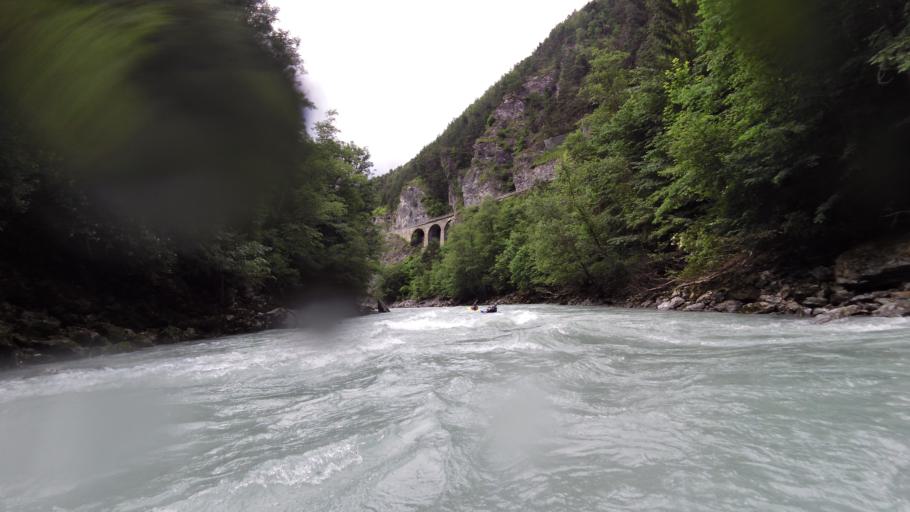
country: AT
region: Tyrol
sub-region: Politischer Bezirk Landeck
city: Landeck
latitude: 47.1290
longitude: 10.5747
